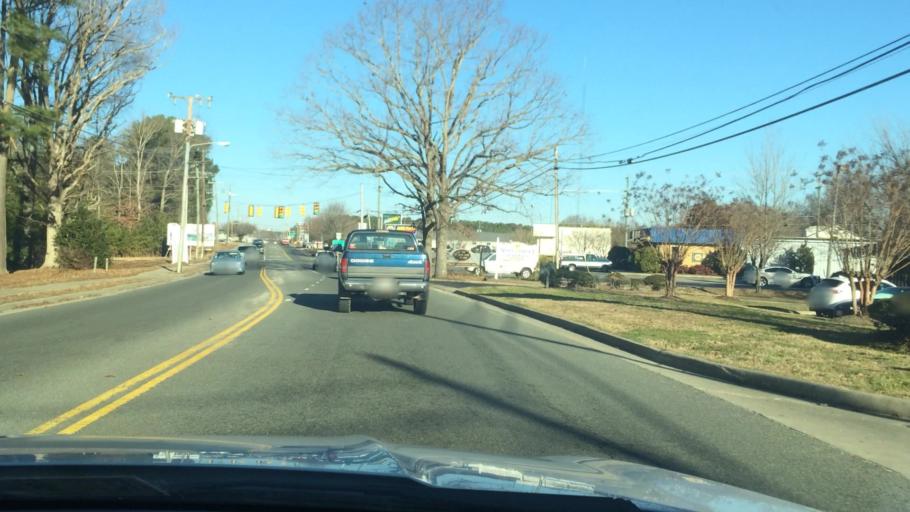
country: US
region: Virginia
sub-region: Lancaster County
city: Kilmarnock
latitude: 37.7170
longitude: -76.3819
